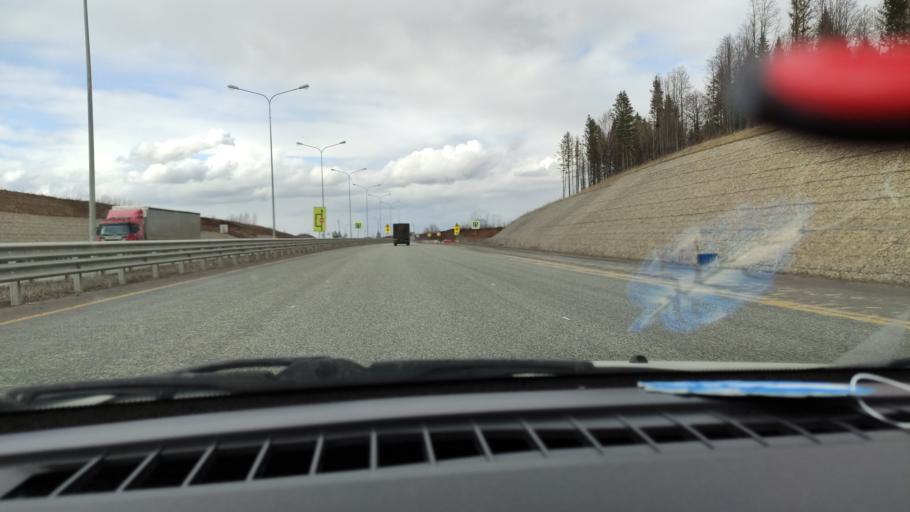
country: RU
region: Perm
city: Lobanovo
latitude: 57.8286
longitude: 56.3008
